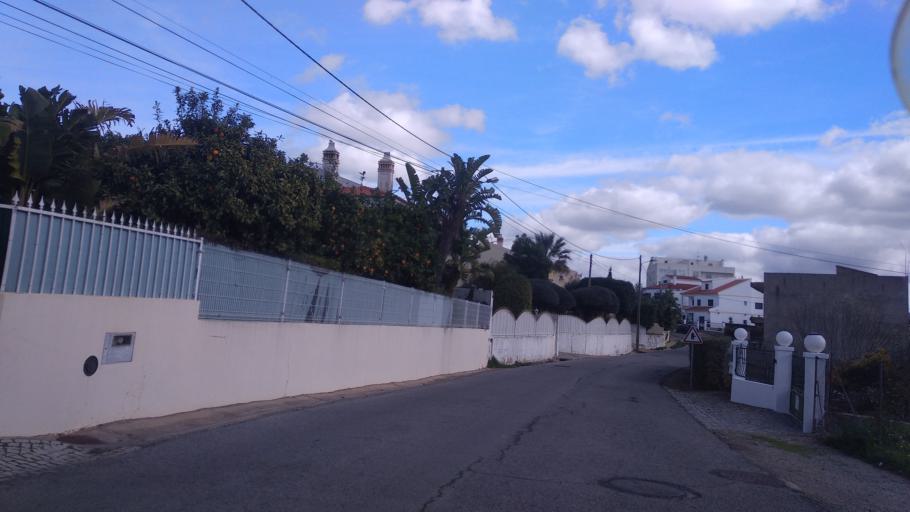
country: PT
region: Faro
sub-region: Sao Bras de Alportel
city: Sao Bras de Alportel
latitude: 37.1505
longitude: -7.8958
